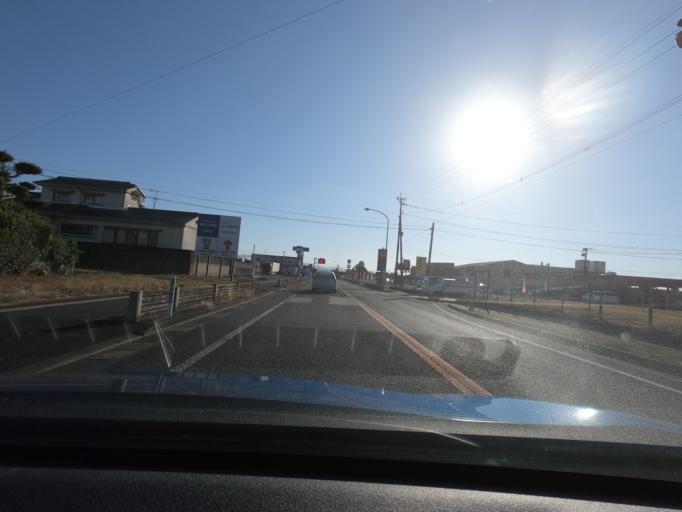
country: JP
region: Kagoshima
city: Izumi
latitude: 32.1265
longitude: 130.3434
